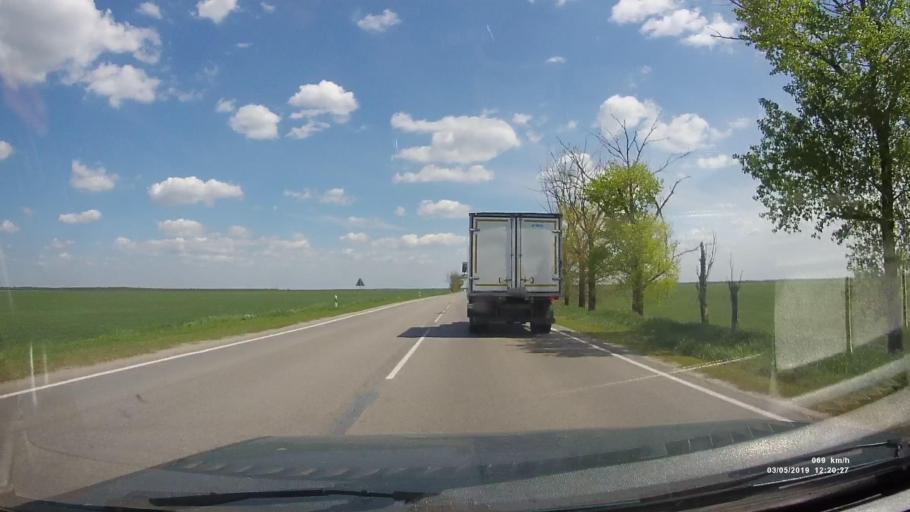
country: RU
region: Rostov
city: Melikhovskaya
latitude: 47.4052
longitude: 40.6242
